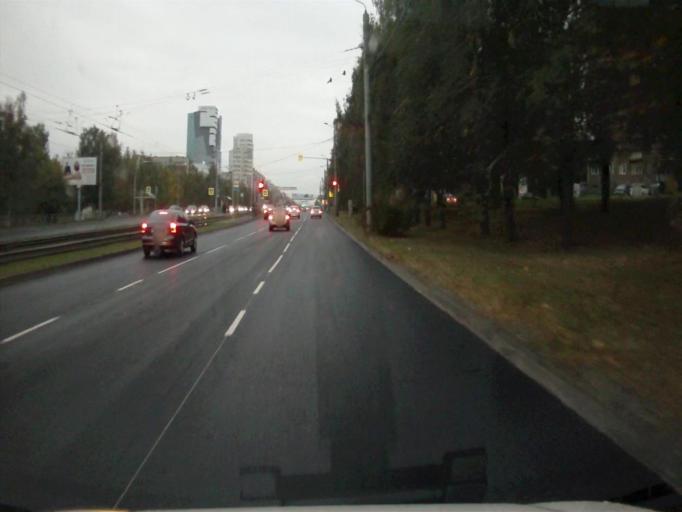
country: RU
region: Chelyabinsk
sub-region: Gorod Chelyabinsk
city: Chelyabinsk
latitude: 55.1891
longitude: 61.3408
